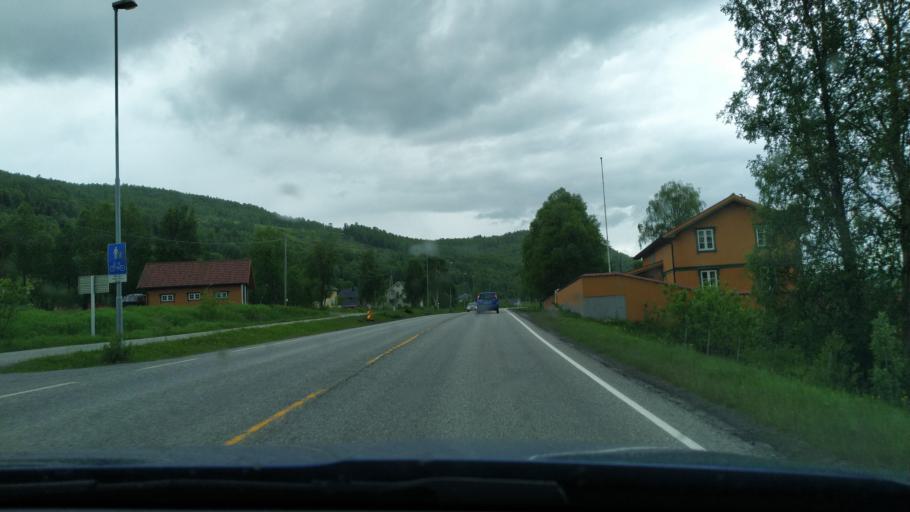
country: NO
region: Troms
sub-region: Malselv
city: Moen
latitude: 69.0146
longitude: 18.4832
